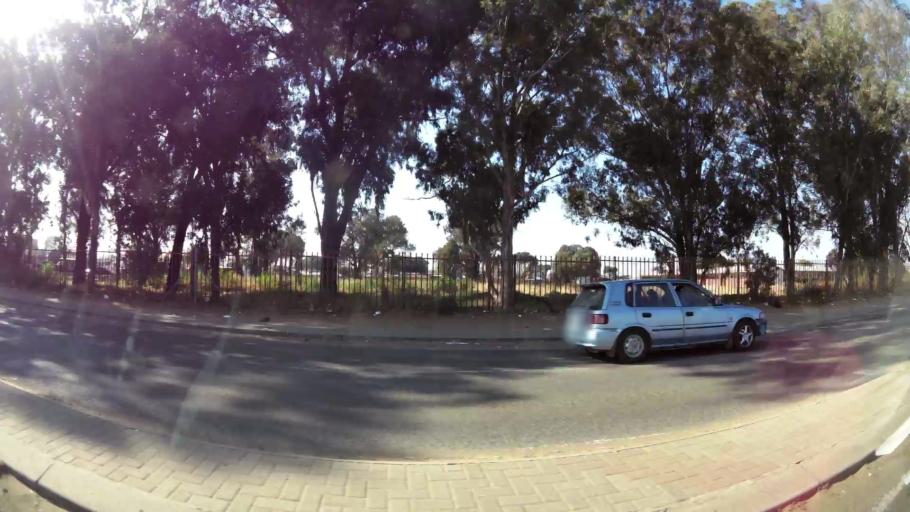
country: ZA
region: Orange Free State
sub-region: Mangaung Metropolitan Municipality
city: Bloemfontein
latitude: -29.1347
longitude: 26.2387
